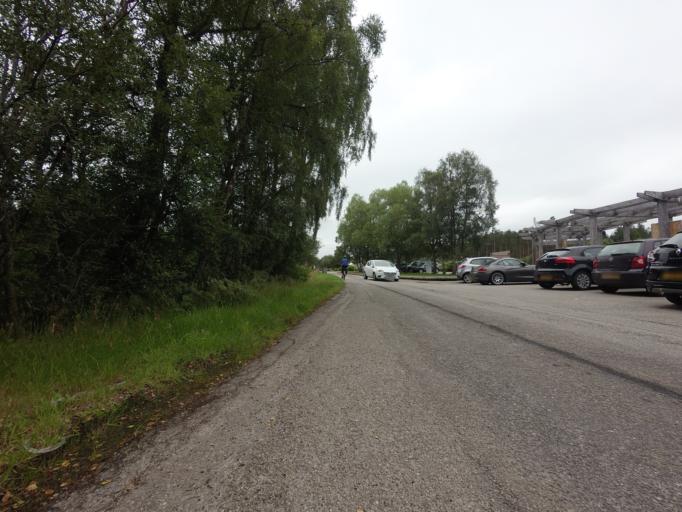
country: GB
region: Scotland
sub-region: Highland
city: Evanton
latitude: 57.9608
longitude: -4.4080
